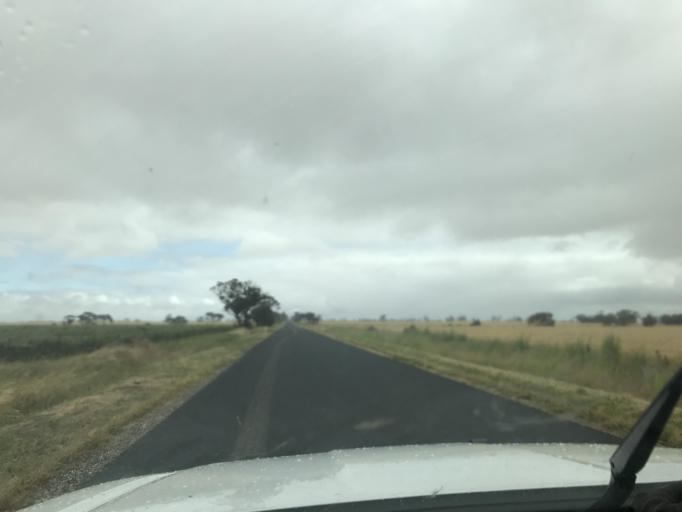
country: AU
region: South Australia
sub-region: Tatiara
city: Bordertown
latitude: -36.2853
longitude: 141.1484
